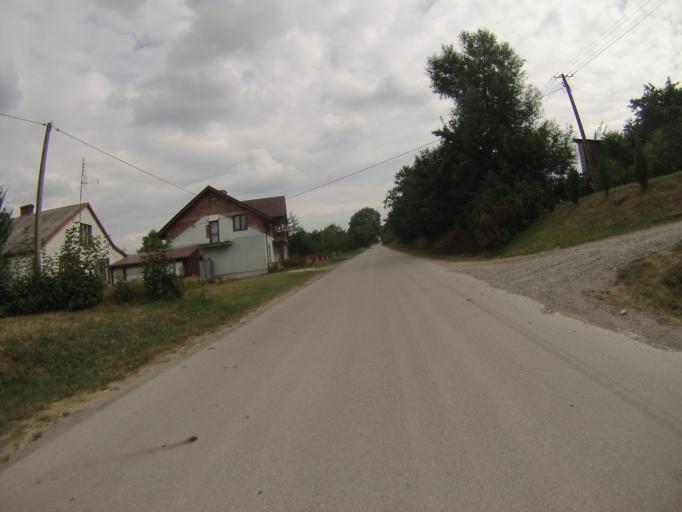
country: PL
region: Swietokrzyskie
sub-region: Powiat kielecki
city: Lagow
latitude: 50.7207
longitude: 21.1154
